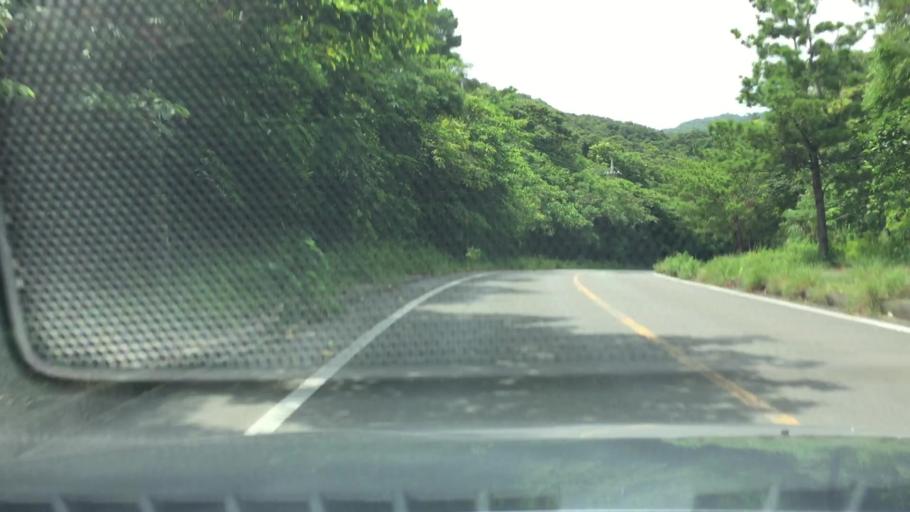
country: JP
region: Okinawa
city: Ishigaki
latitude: 24.4268
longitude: 124.2109
